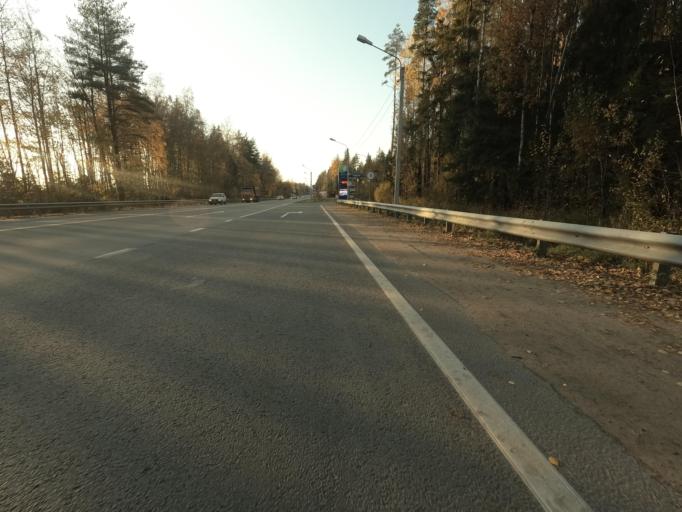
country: RU
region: St.-Petersburg
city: Pesochnyy
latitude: 60.1799
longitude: 30.1404
